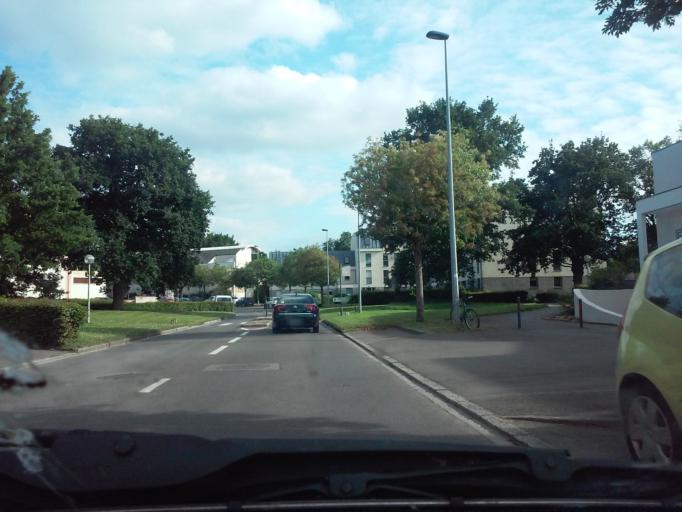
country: FR
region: Brittany
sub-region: Departement d'Ille-et-Vilaine
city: Saint-Jacques-de-la-Lande
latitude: 48.0993
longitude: -1.7113
